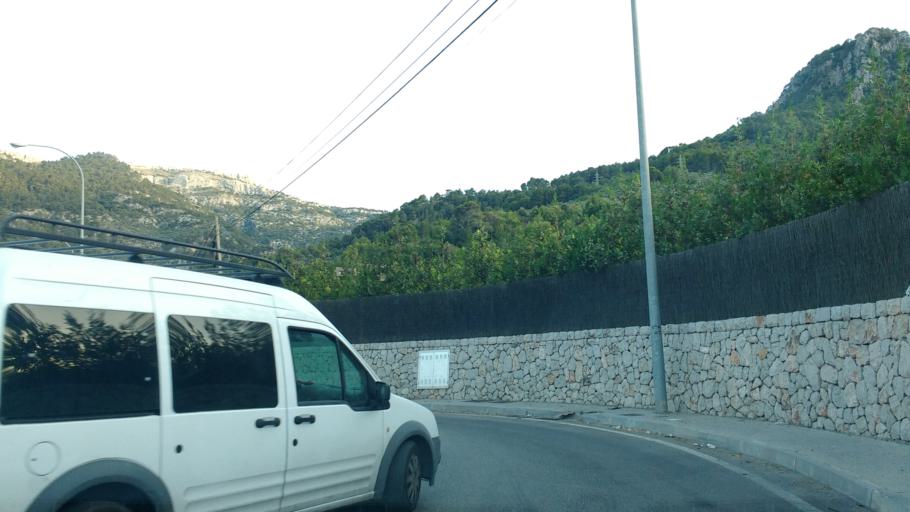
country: ES
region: Balearic Islands
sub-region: Illes Balears
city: Soller
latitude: 39.7669
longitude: 2.7078
